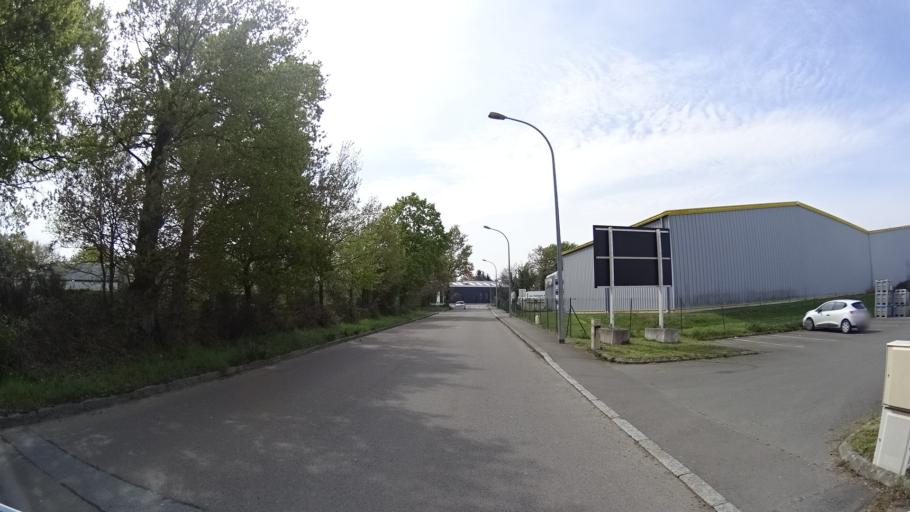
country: FR
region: Brittany
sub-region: Departement d'Ille-et-Vilaine
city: Chartres-de-Bretagne
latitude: 48.0357
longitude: -1.7254
